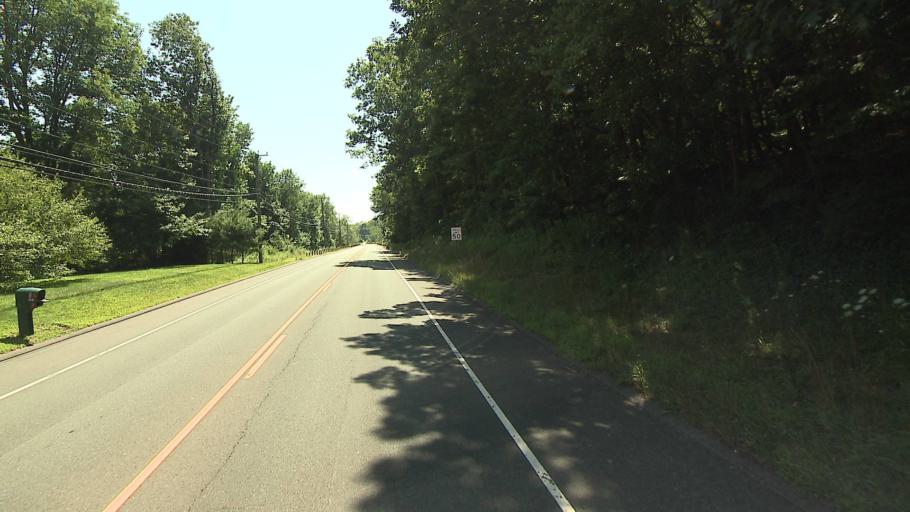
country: US
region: Connecticut
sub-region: Litchfield County
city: Northwest Harwinton
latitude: 41.7784
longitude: -73.0685
